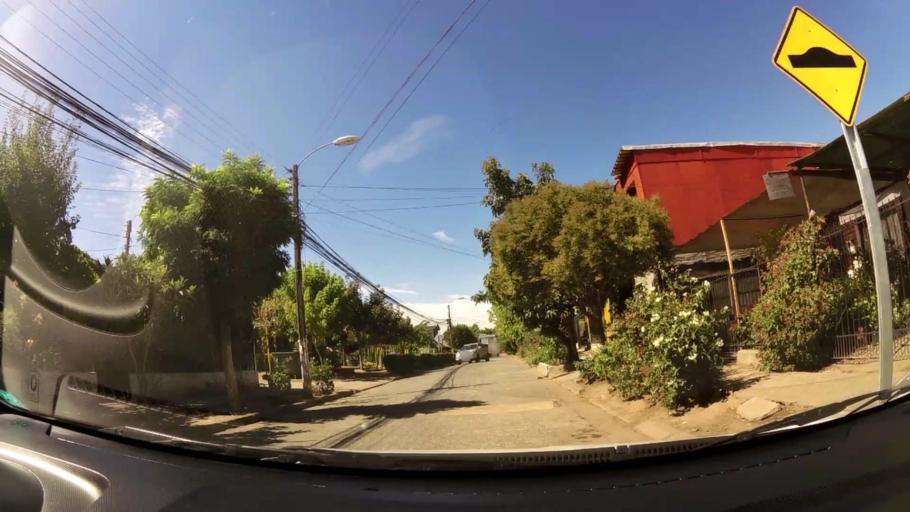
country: CL
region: O'Higgins
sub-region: Provincia de Cachapoal
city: Graneros
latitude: -33.9736
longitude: -70.7103
